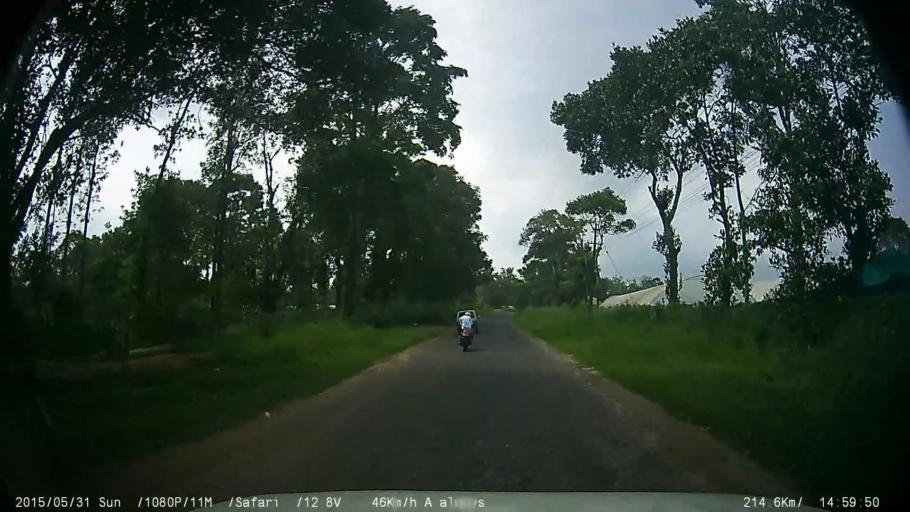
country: IN
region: Kerala
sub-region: Wayanad
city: Kalpetta
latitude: 11.6124
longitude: 76.2113
